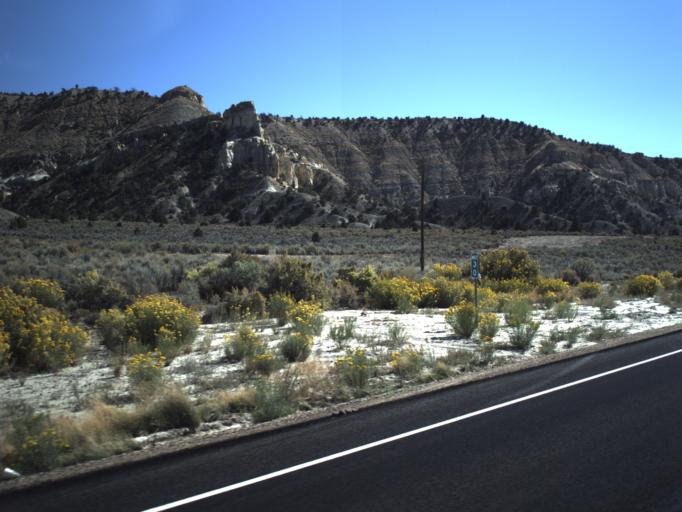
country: US
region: Utah
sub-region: Garfield County
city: Panguitch
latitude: 37.5732
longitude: -111.9881
